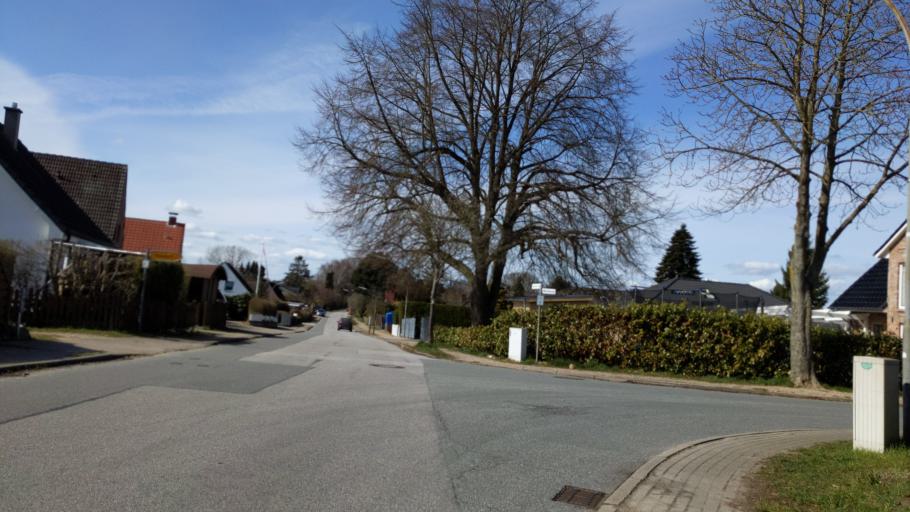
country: DE
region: Schleswig-Holstein
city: Ratekau
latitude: 53.9686
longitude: 10.7011
